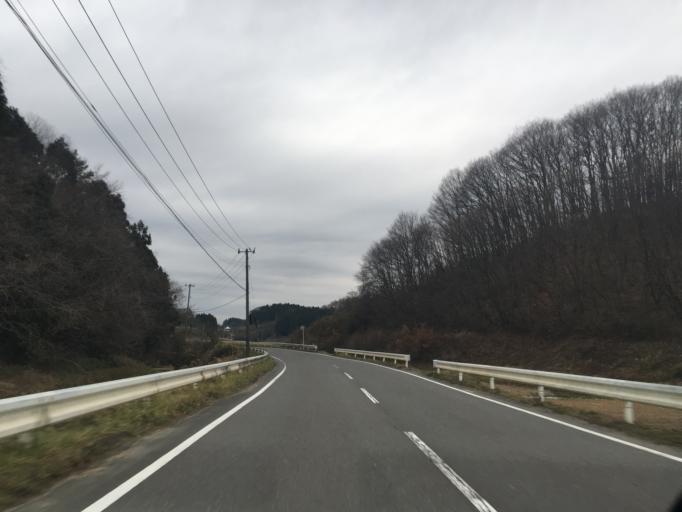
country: JP
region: Fukushima
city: Koriyama
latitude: 37.3501
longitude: 140.4457
